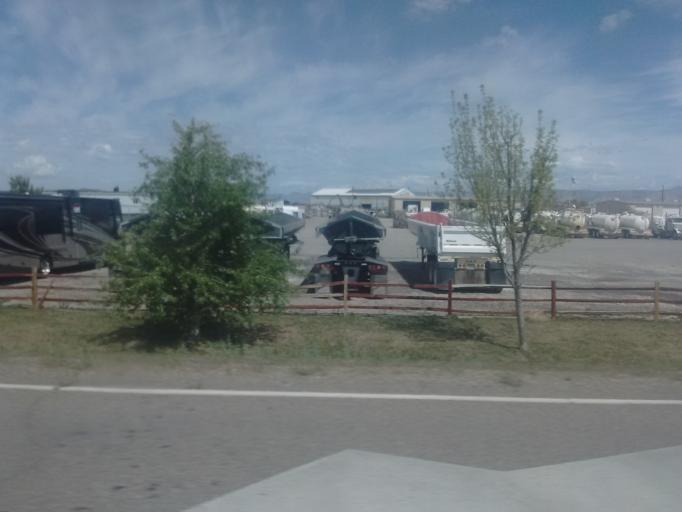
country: US
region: Colorado
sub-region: Mesa County
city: Redlands
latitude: 39.0902
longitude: -108.6145
